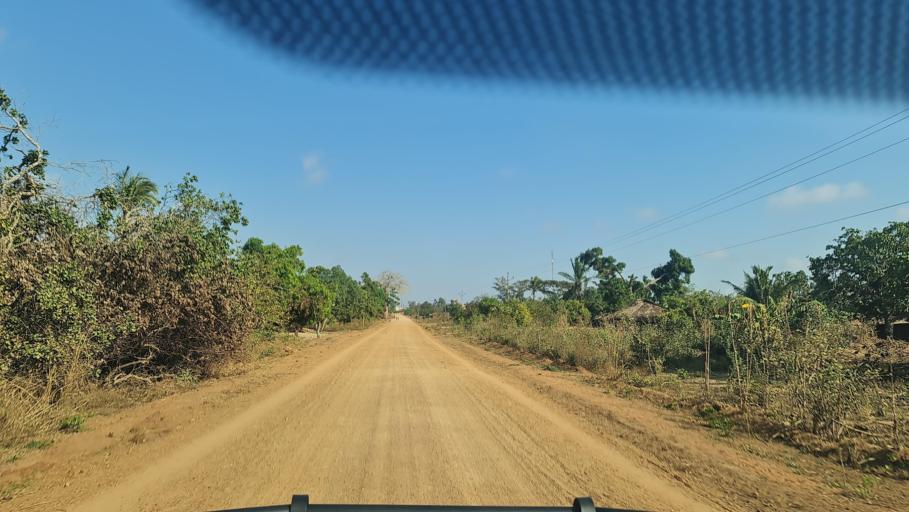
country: MZ
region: Nampula
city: Ilha de Mocambique
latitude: -15.2925
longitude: 40.1183
